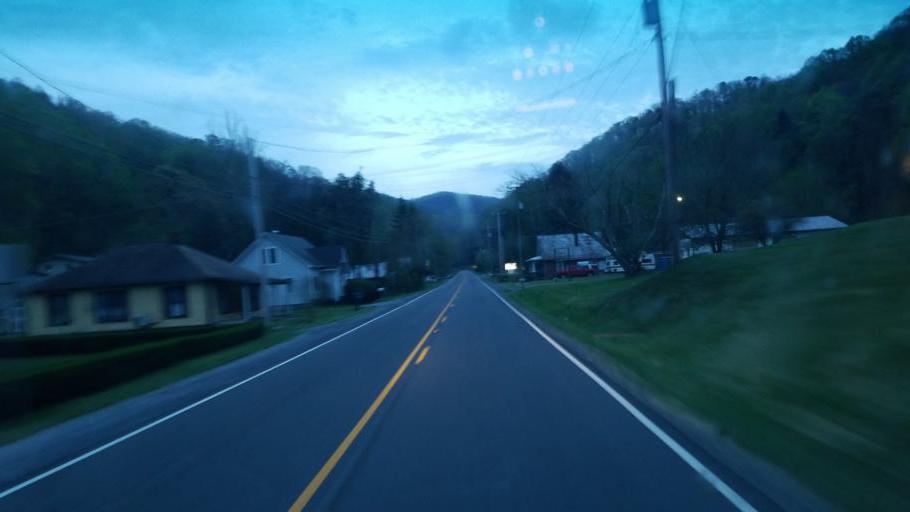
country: US
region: Virginia
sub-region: Smyth County
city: Marion
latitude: 36.8165
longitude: -81.4685
